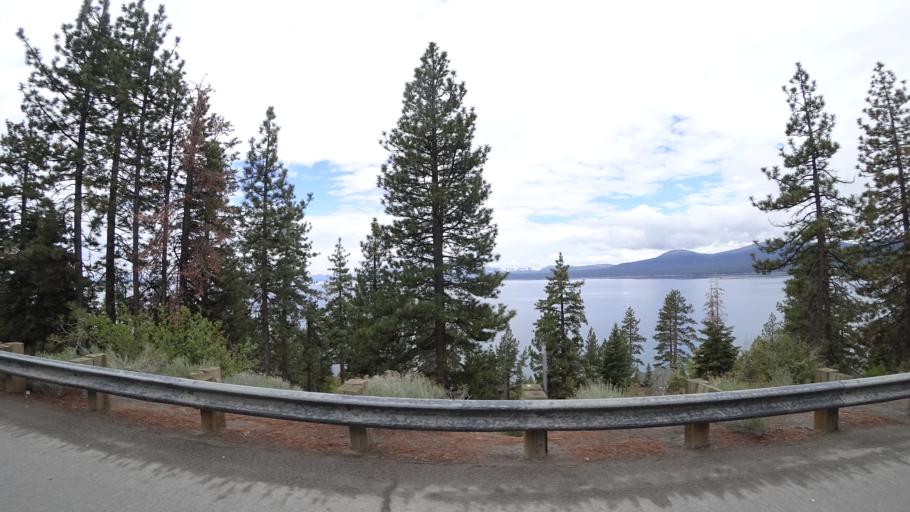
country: US
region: California
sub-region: Placer County
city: Kings Beach
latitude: 39.2294
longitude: -120.0135
